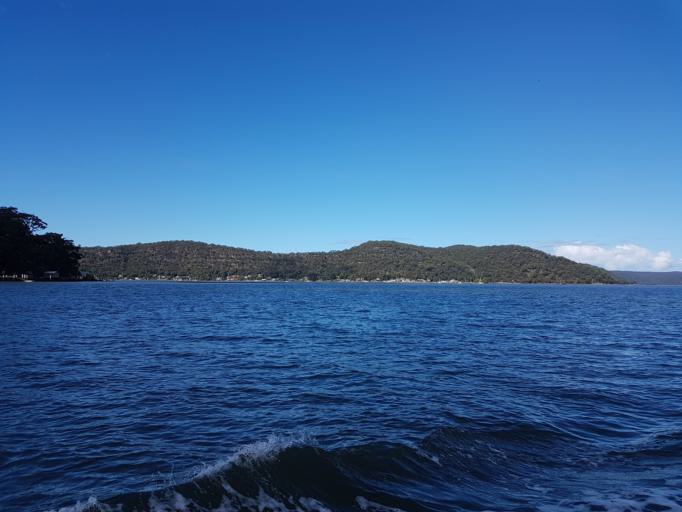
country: AU
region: New South Wales
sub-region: Gosford Shire
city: Umina
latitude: -33.5426
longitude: 151.2331
